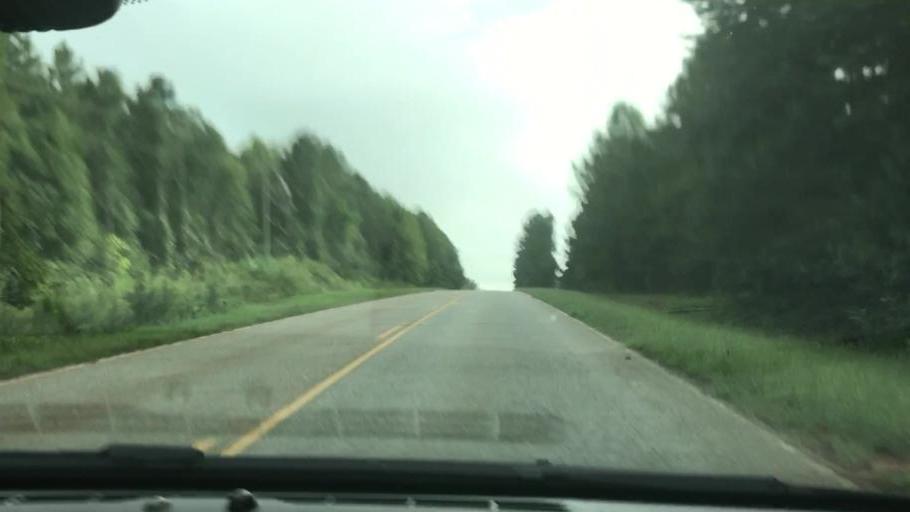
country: US
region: Georgia
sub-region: Quitman County
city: Georgetown
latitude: 31.9164
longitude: -85.0270
